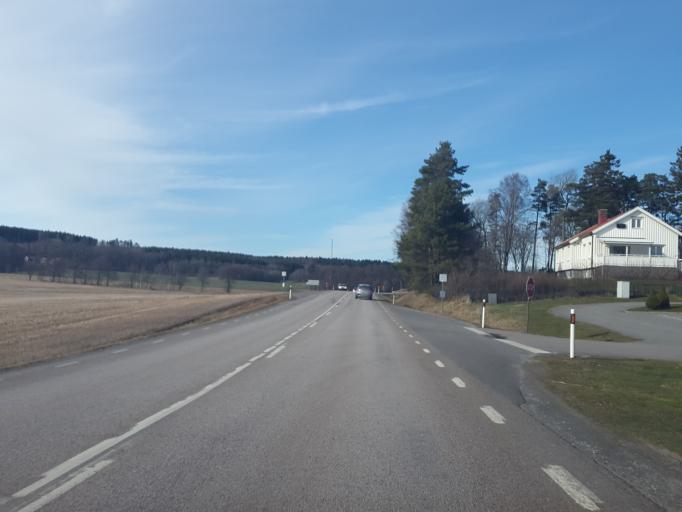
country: SE
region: Vaestra Goetaland
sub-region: Vargarda Kommun
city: Jonstorp
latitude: 58.0085
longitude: 12.6269
